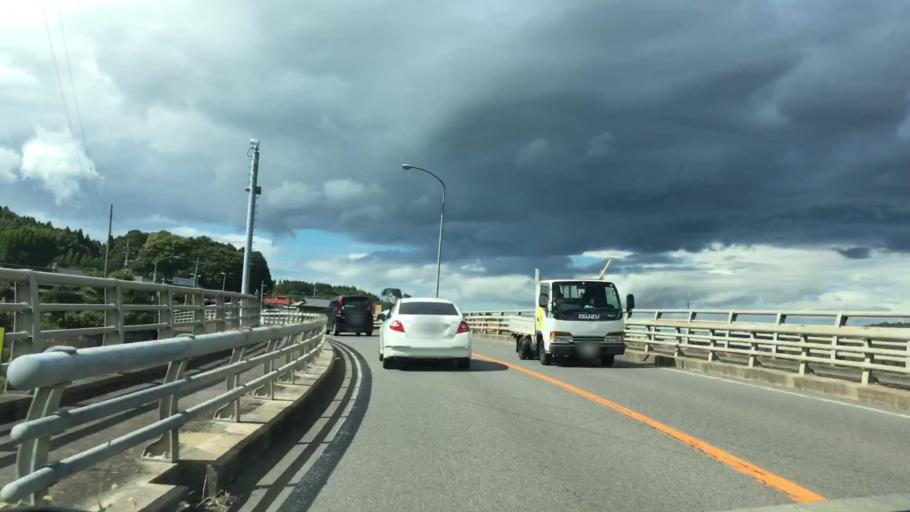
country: JP
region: Saga Prefecture
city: Imaricho-ko
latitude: 33.2408
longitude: 129.8509
